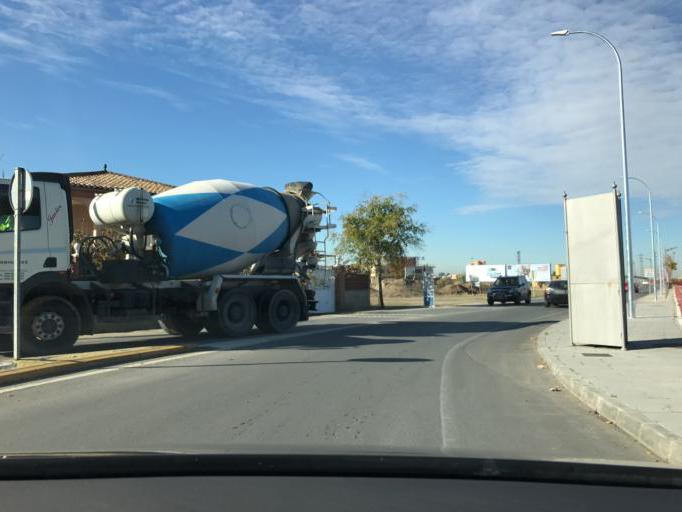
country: ES
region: Andalusia
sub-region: Provincia de Granada
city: Churriana de la Vega
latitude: 37.1482
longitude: -3.6556
